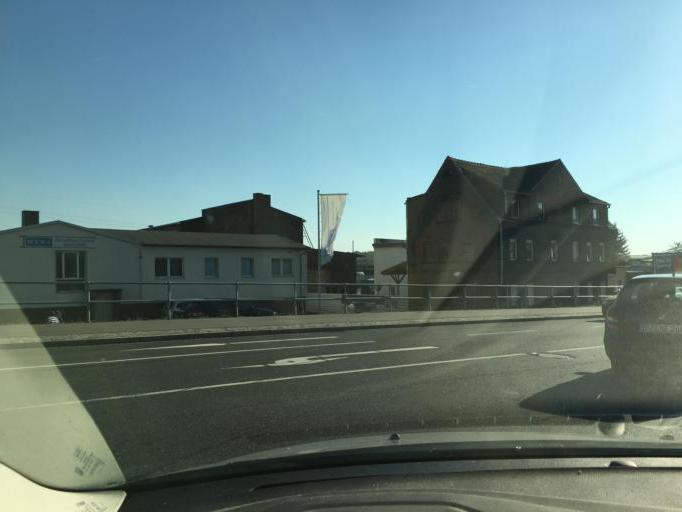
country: DE
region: Saxony
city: Bitterfeld-Wolfen
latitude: 51.6159
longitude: 12.3132
